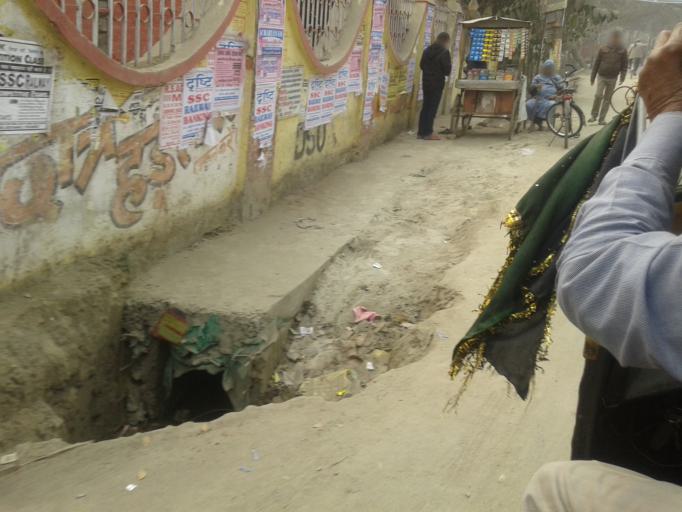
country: IN
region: Bihar
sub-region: Muzaffarpur
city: Muzaffarpur
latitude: 26.1157
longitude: 85.3797
